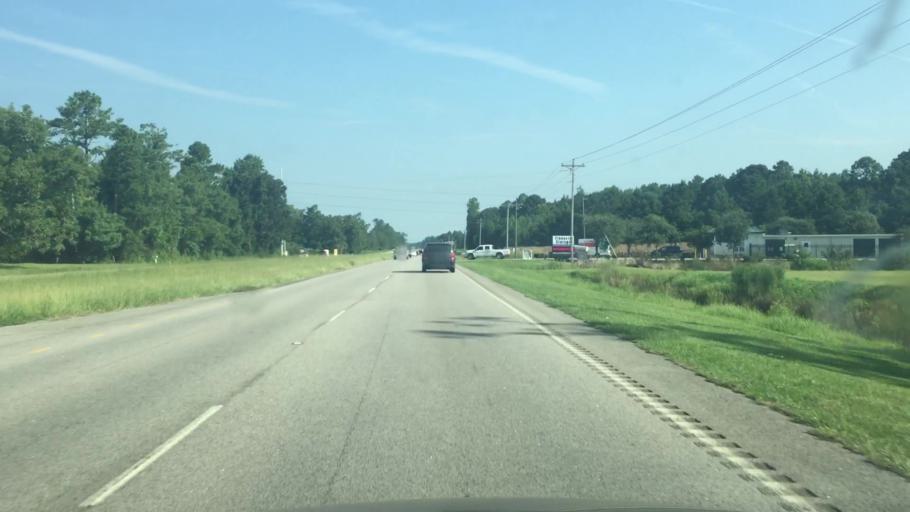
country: US
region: South Carolina
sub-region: Horry County
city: Little River
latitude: 33.9632
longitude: -78.7383
